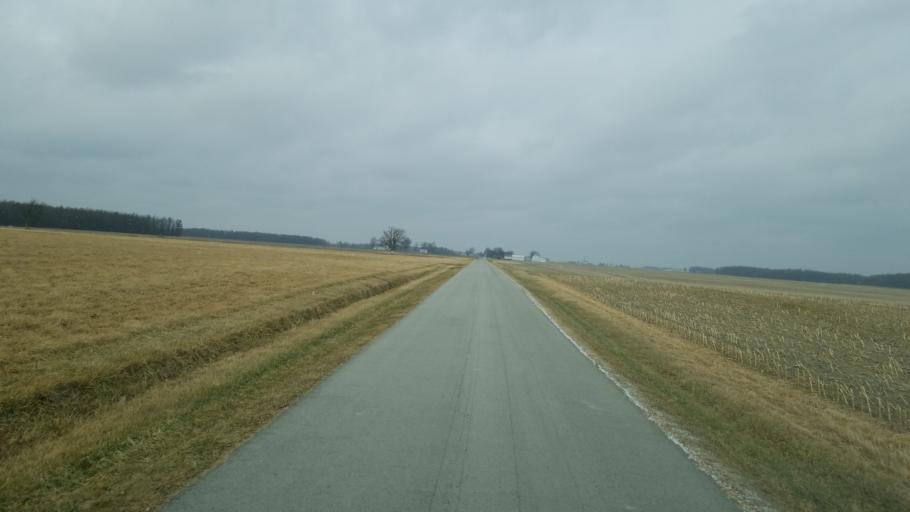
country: US
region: Ohio
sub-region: Hardin County
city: Forest
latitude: 40.7495
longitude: -83.4777
